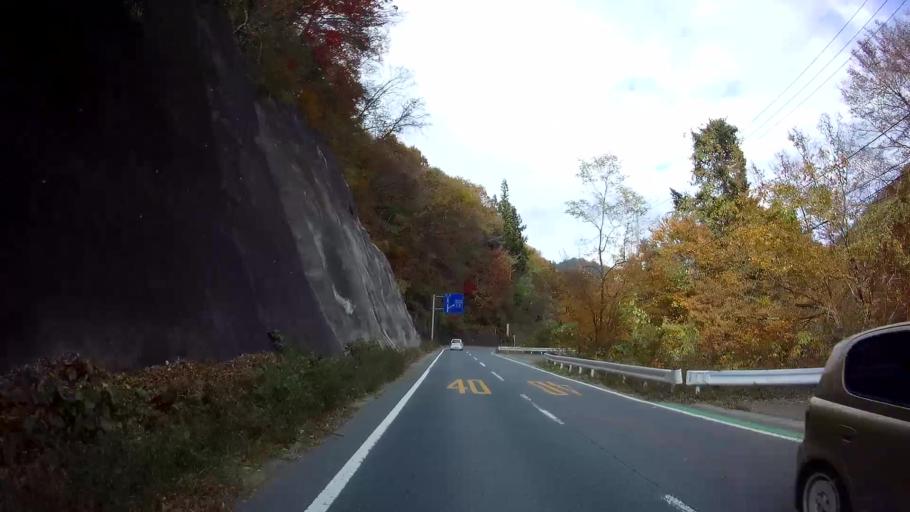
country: JP
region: Gunma
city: Nakanojomachi
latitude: 36.6127
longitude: 138.6398
